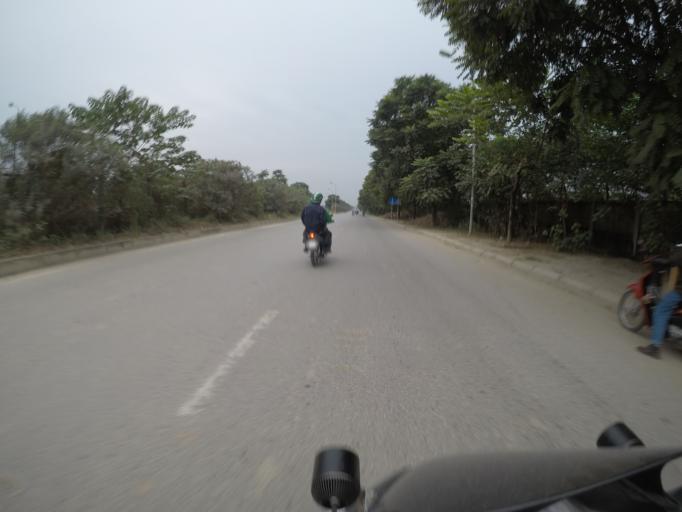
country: VN
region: Ha Noi
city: Cau Dien
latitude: 21.0071
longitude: 105.7618
